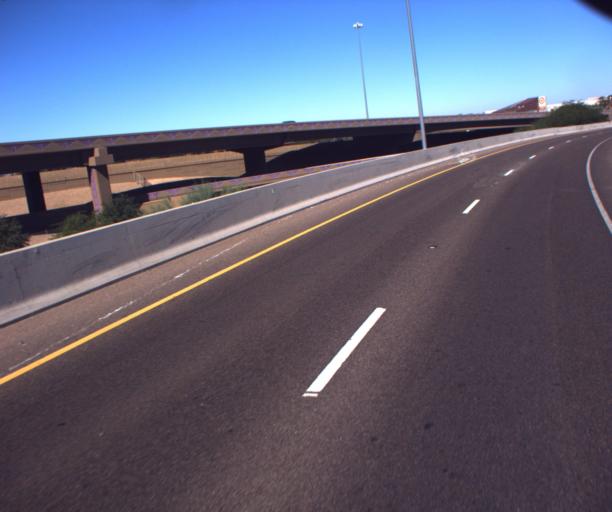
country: US
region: Arizona
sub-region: Maricopa County
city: Chandler
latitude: 33.2940
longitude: -111.8932
